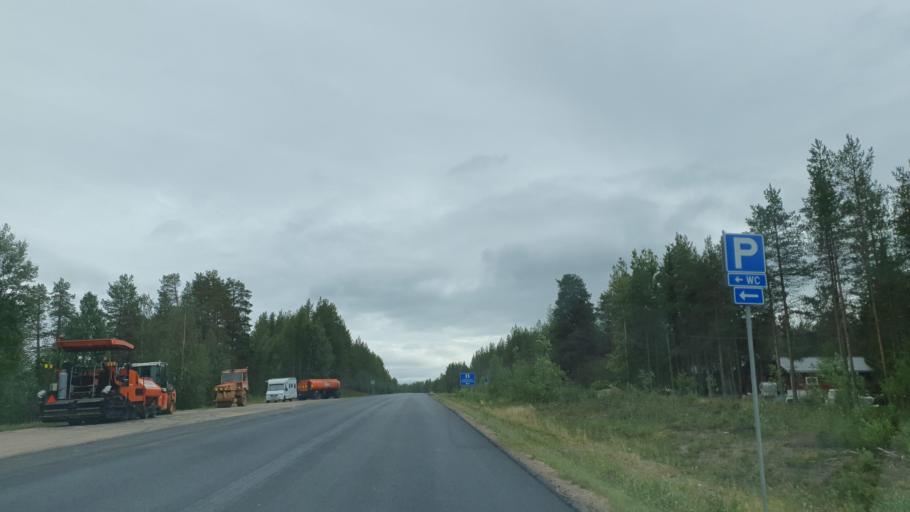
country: FI
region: Lapland
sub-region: Rovaniemi
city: Rovaniemi
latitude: 66.7916
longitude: 25.4158
